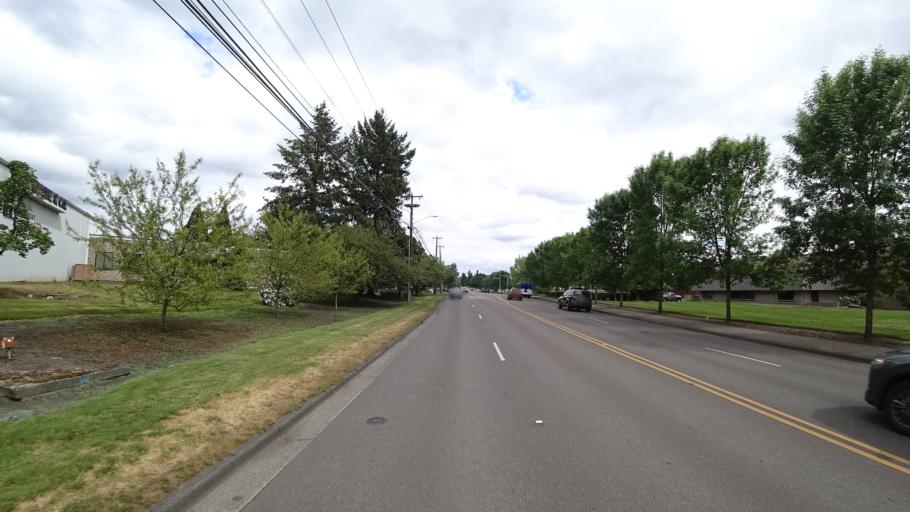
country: US
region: Oregon
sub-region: Washington County
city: Raleigh Hills
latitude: 45.4755
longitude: -122.7803
